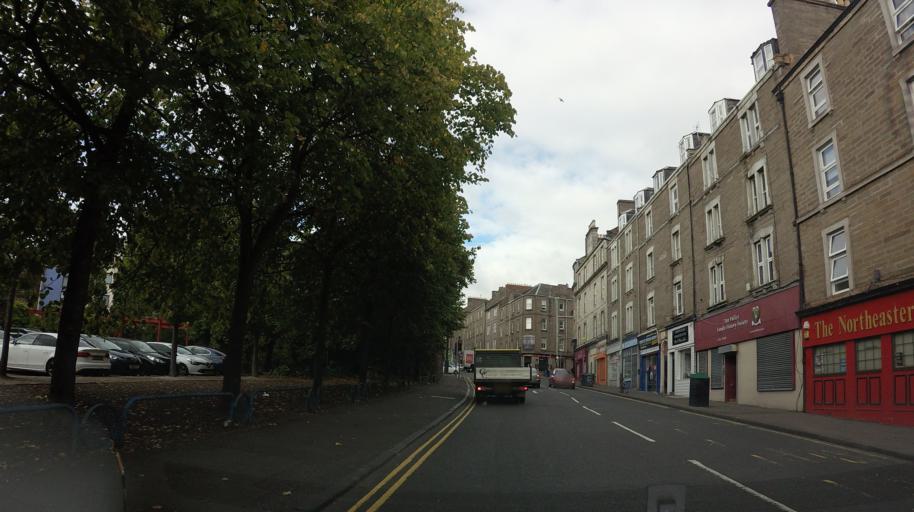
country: GB
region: Scotland
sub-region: Dundee City
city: Dundee
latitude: 56.4674
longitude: -2.9583
